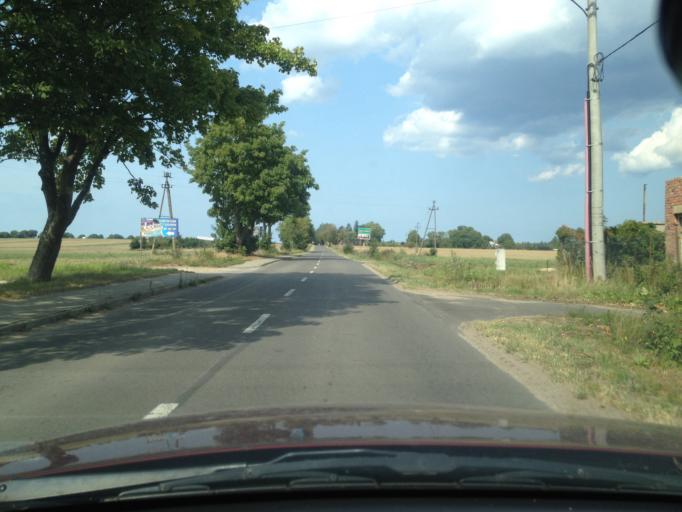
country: PL
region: West Pomeranian Voivodeship
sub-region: Powiat gryficki
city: Pobierowo
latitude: 54.0138
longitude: 14.8694
